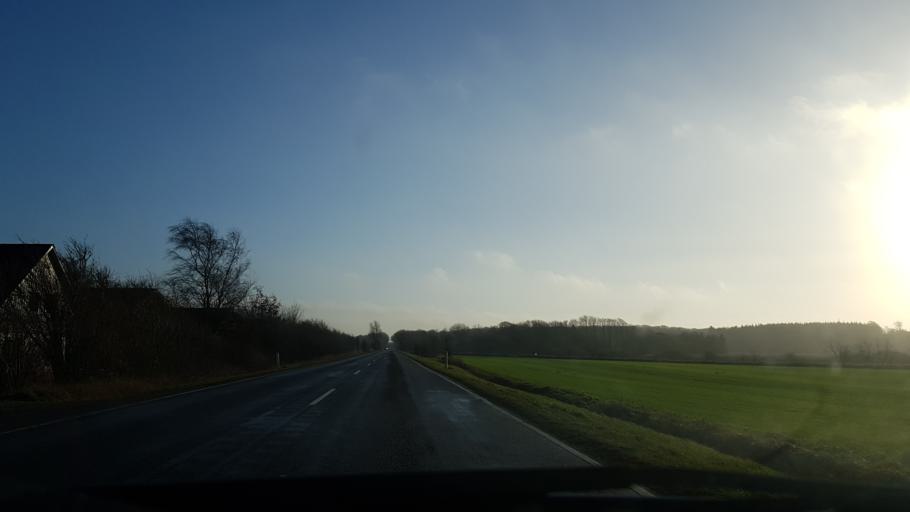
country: DK
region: South Denmark
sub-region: Tonder Kommune
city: Toftlund
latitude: 55.2301
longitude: 9.1697
